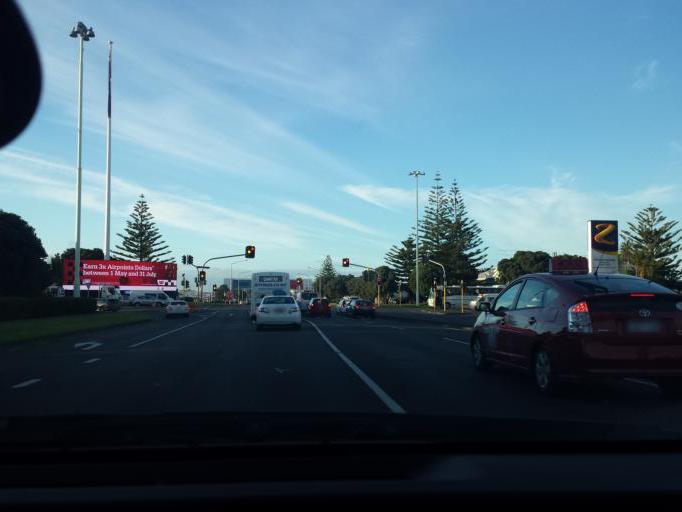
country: NZ
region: Auckland
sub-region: Auckland
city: Mangere
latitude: -37.0011
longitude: 174.7890
